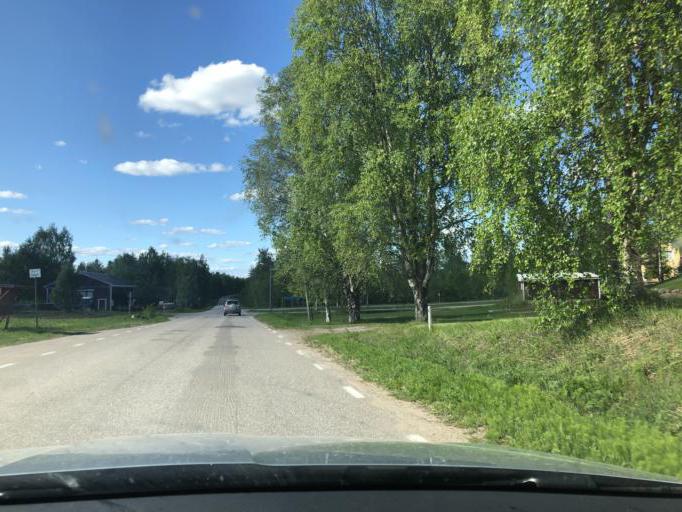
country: SE
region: Norrbotten
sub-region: Kalix Kommun
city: Kalix
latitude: 65.9262
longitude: 23.1640
